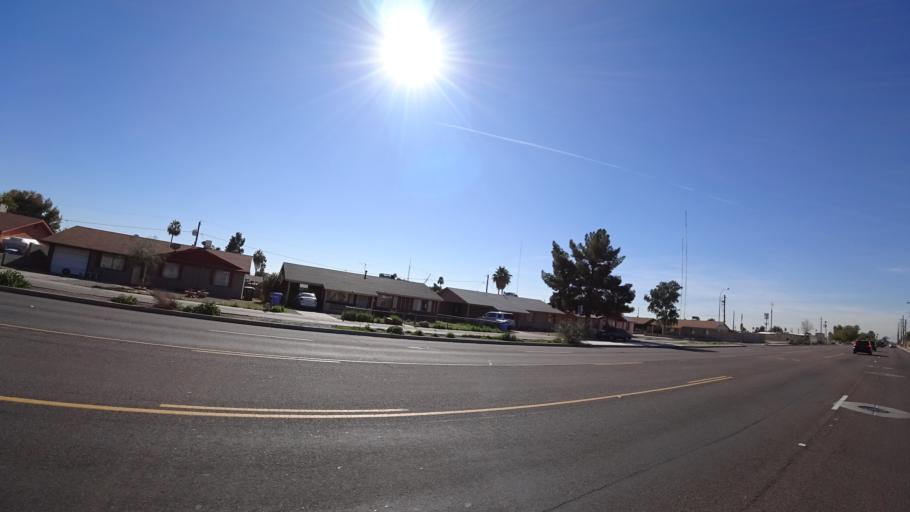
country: US
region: Arizona
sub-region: Maricopa County
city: Glendale
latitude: 33.5092
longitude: -112.2158
